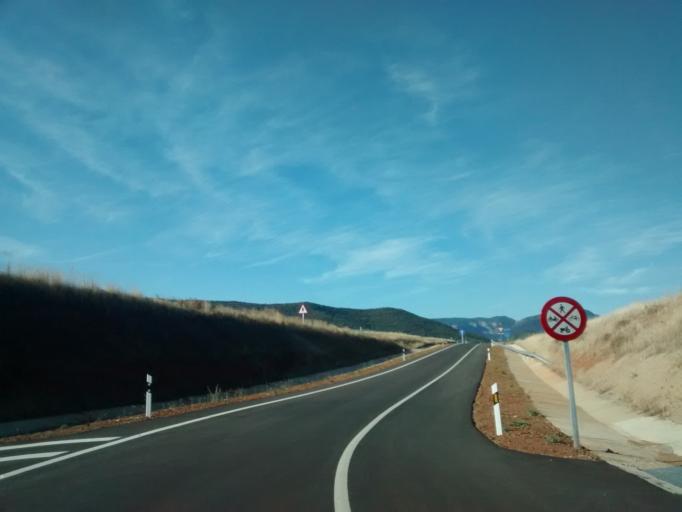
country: ES
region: Aragon
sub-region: Provincia de Huesca
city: Jaca
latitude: 42.5650
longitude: -0.6018
